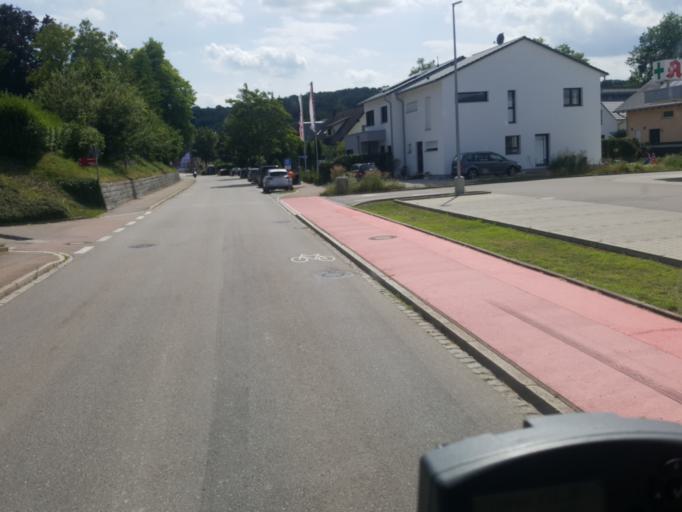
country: DE
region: Baden-Wuerttemberg
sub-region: Freiburg Region
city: Schliengen
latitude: 47.7586
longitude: 7.5775
